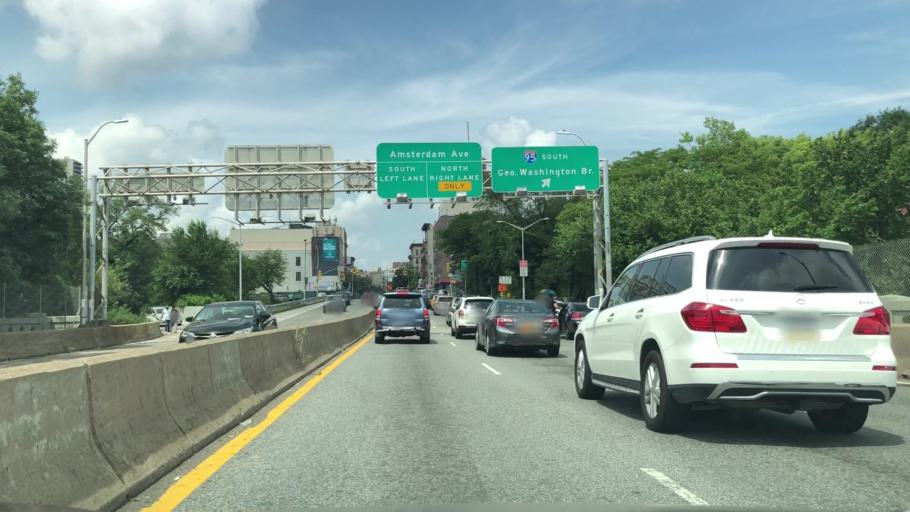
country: US
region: New York
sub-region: New York County
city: Inwood
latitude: 40.8474
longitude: -73.9291
